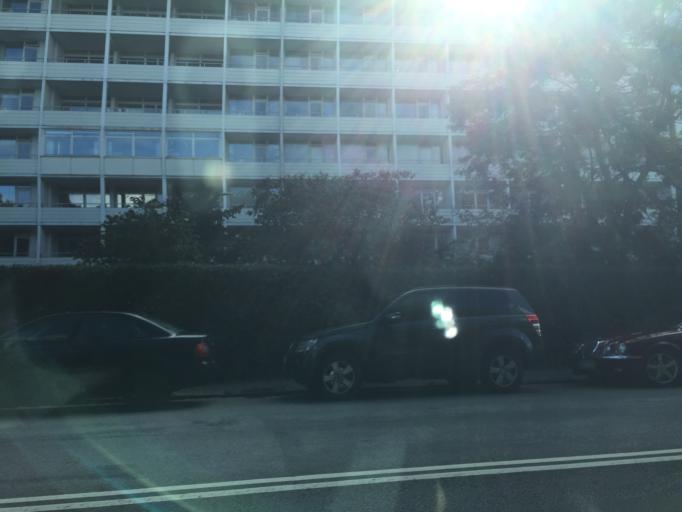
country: SE
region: Skane
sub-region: Malmo
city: Malmoe
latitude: 55.5912
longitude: 12.9977
